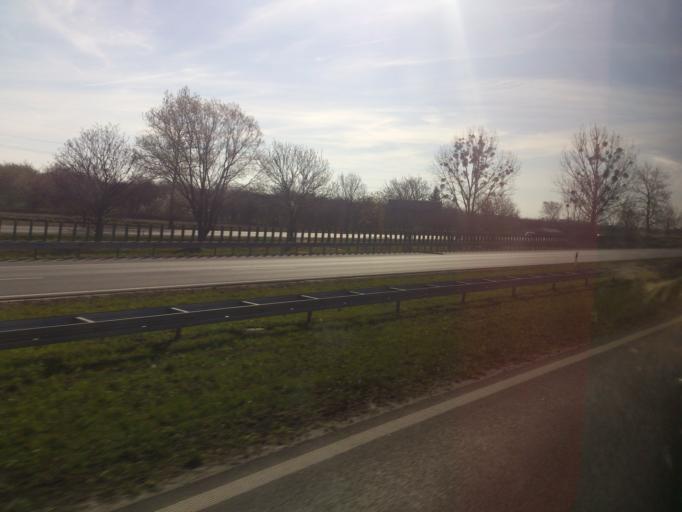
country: PL
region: Kujawsko-Pomorskie
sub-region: Powiat aleksandrowski
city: Raciazek
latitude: 52.8405
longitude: 18.7930
